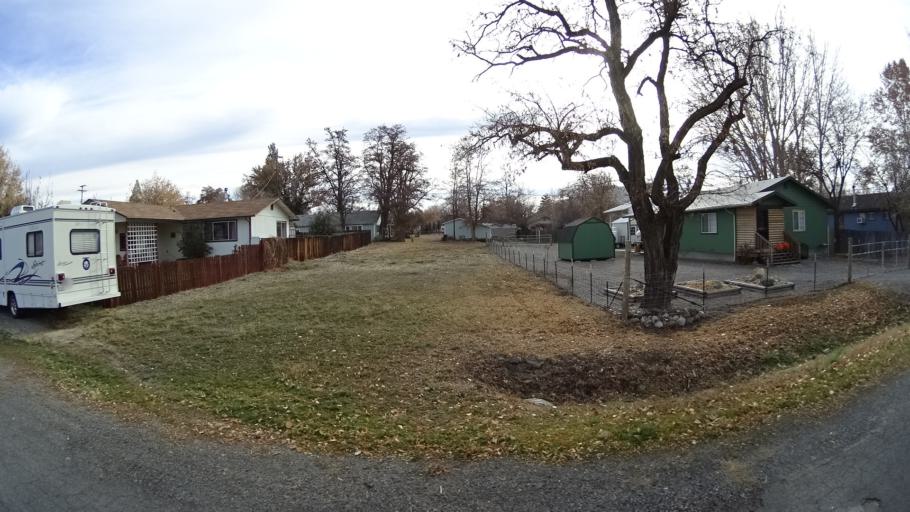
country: US
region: California
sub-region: Siskiyou County
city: Montague
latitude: 41.7303
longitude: -122.5311
